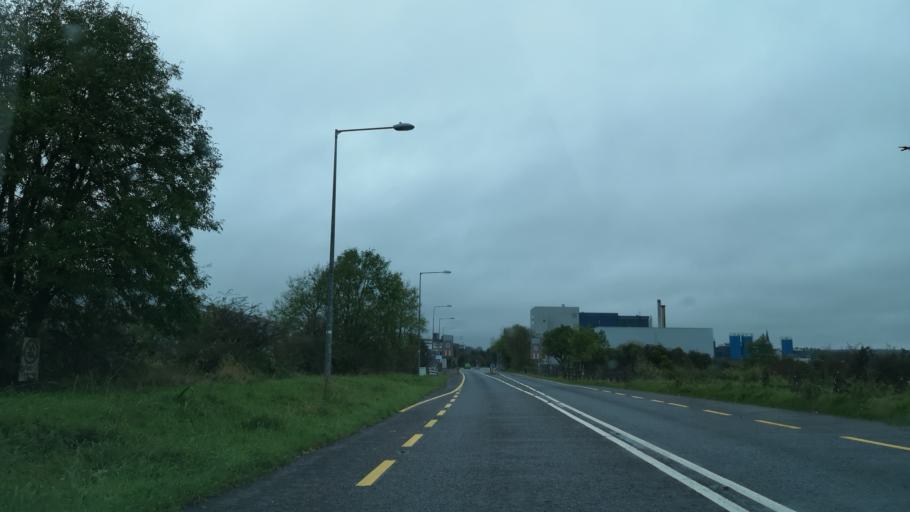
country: IE
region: Connaught
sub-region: Roscommon
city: Ballaghaderreen
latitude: 53.8964
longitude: -8.5641
